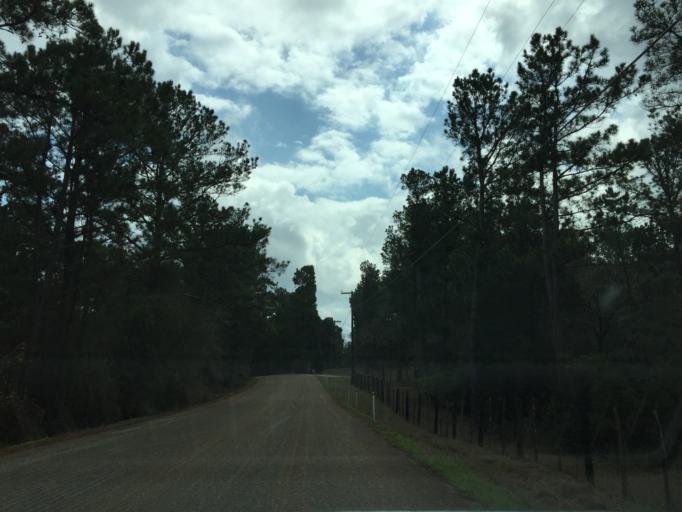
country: US
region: Texas
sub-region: Bastrop County
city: Bastrop
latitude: 30.1283
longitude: -97.2834
